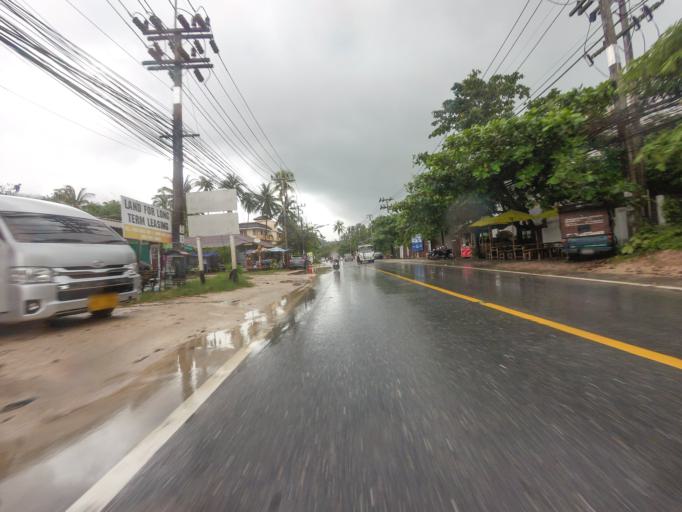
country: TH
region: Surat Thani
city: Ko Samui
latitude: 9.4462
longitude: 100.0258
